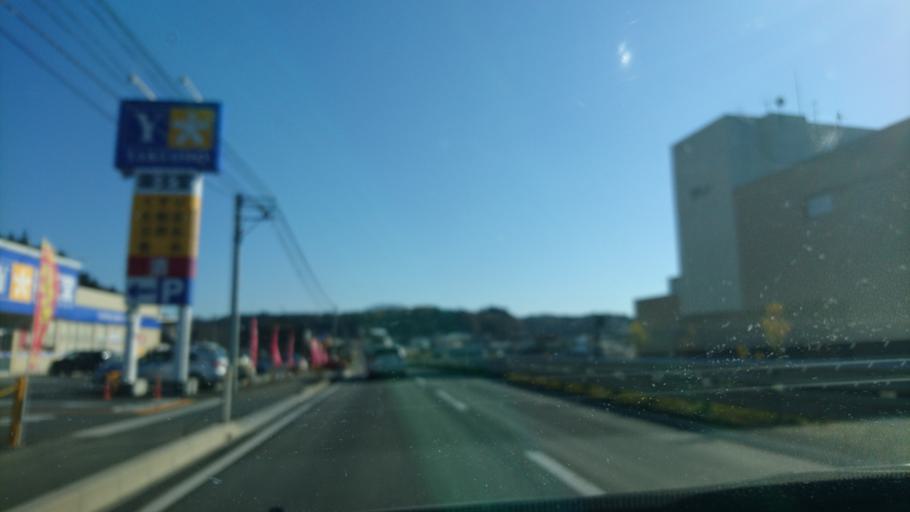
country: JP
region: Iwate
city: Ichinoseki
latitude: 38.9961
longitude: 141.3219
